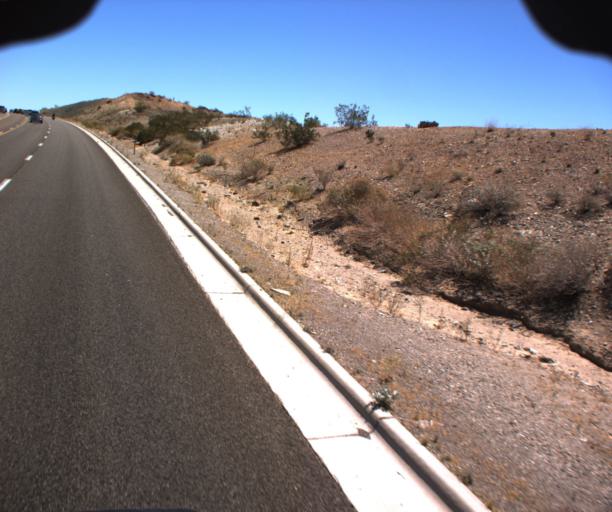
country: US
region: Arizona
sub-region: Mohave County
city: Lake Havasu City
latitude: 34.4527
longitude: -114.3211
